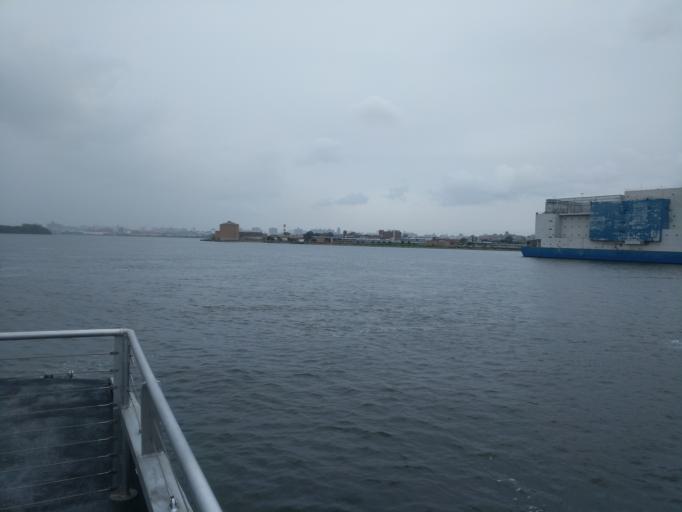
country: US
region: New York
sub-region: Bronx
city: The Bronx
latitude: 40.7989
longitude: -73.8764
